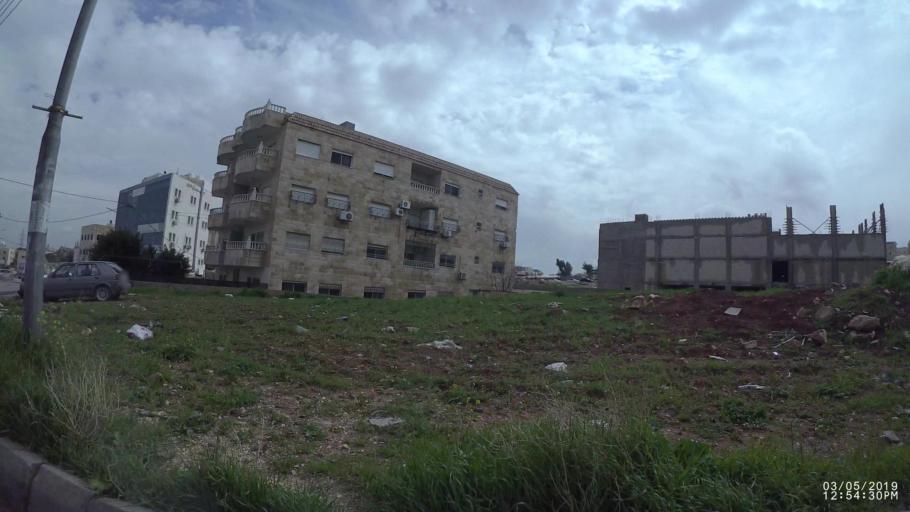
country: JO
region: Amman
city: Amman
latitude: 31.9912
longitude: 35.9427
